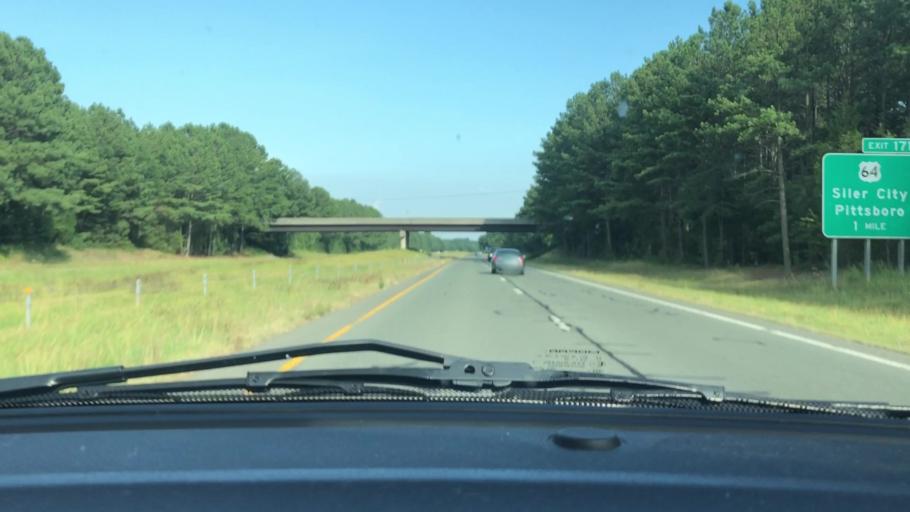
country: US
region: North Carolina
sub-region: Chatham County
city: Siler City
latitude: 35.7491
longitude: -79.4479
